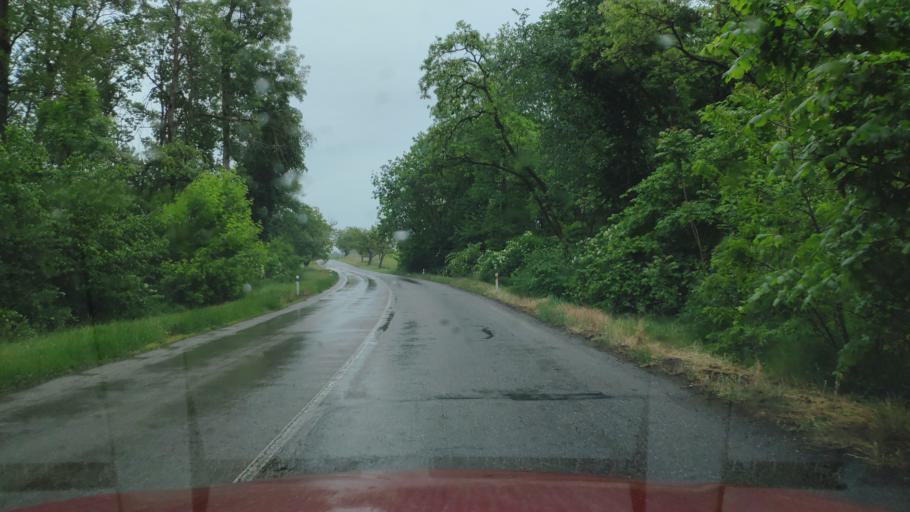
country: HU
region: Borsod-Abauj-Zemplen
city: Ricse
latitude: 48.4350
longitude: 21.9539
